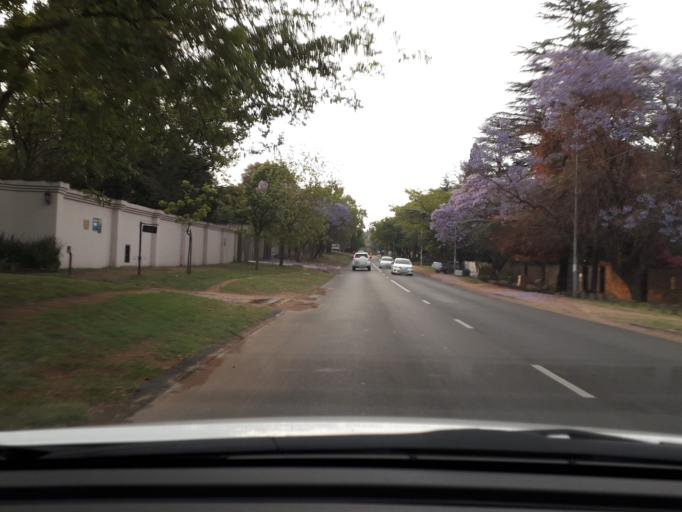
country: ZA
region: Gauteng
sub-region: City of Johannesburg Metropolitan Municipality
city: Midrand
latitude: -26.0539
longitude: 28.0411
